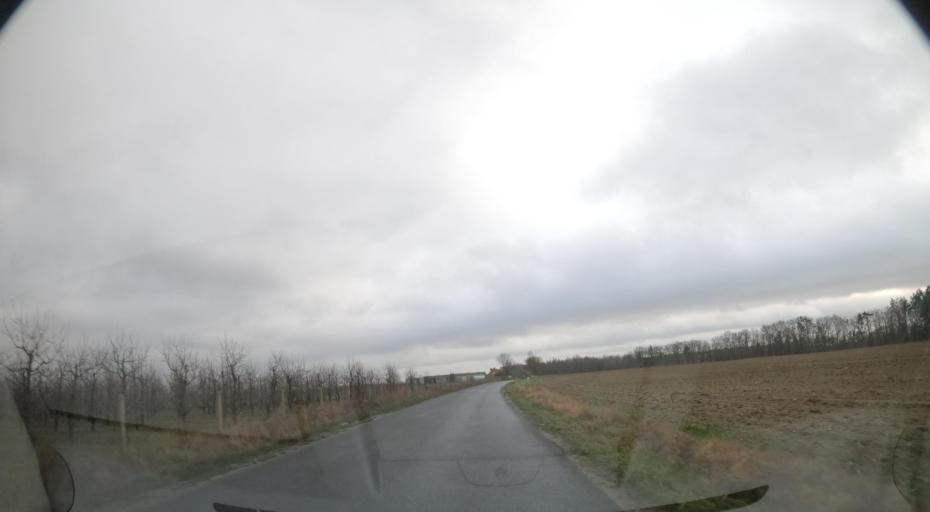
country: PL
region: Greater Poland Voivodeship
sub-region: Powiat pilski
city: Lobzenica
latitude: 53.2435
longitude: 17.2971
